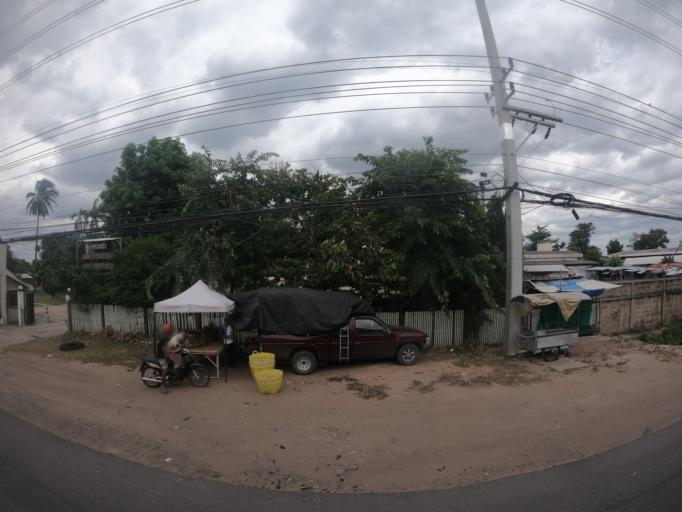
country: TH
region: Nakhon Ratchasima
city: Nakhon Ratchasima
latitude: 14.9470
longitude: 102.1269
